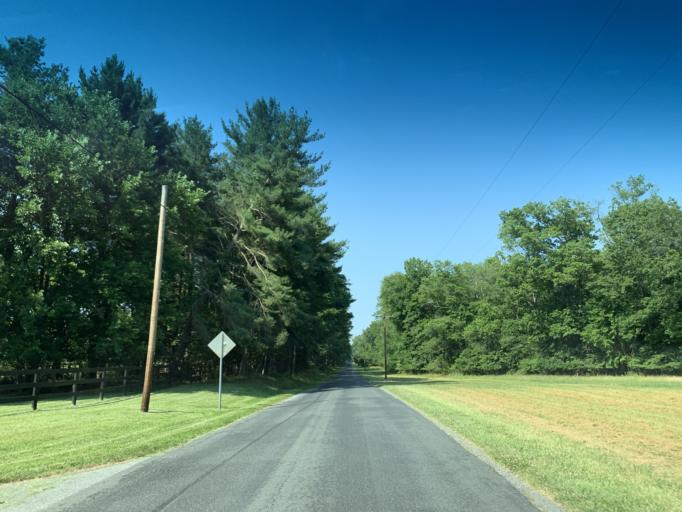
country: US
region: Virginia
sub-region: Loudoun County
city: University Center
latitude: 39.1115
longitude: -77.4634
